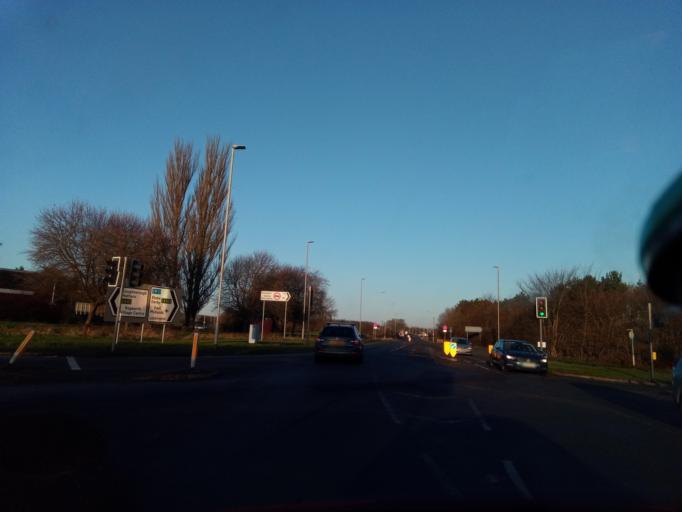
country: GB
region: England
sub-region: Leicestershire
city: Kegworth
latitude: 52.8394
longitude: -1.2863
